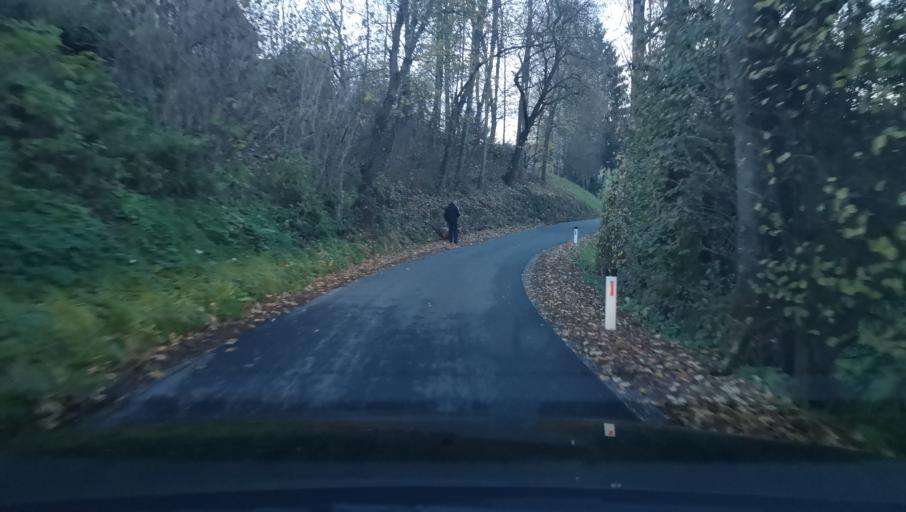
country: AT
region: Styria
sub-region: Politischer Bezirk Weiz
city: Birkfeld
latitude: 47.3380
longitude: 15.6834
